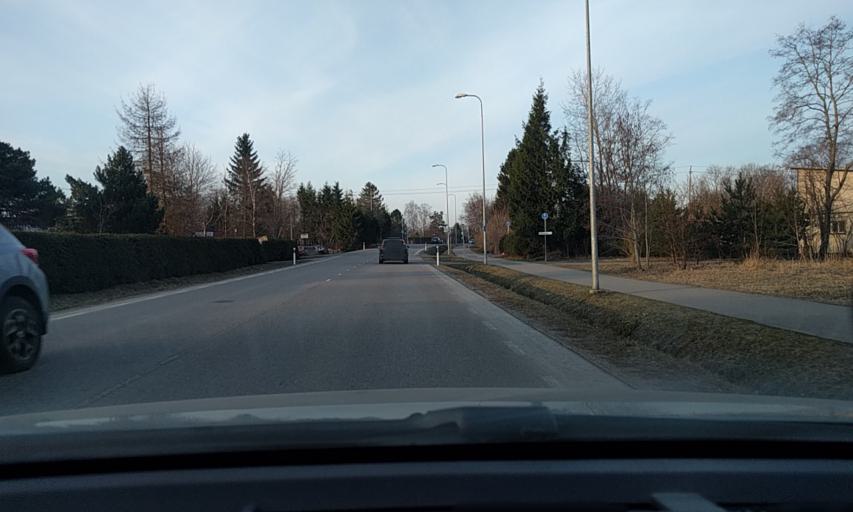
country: EE
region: Harju
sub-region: Viimsi vald
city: Viimsi
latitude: 59.4953
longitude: 24.8952
